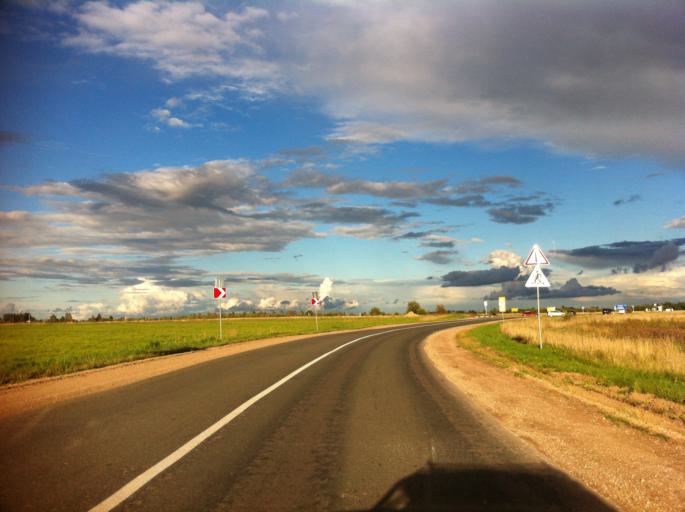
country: RU
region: Pskov
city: Izborsk
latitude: 57.8396
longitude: 28.0081
